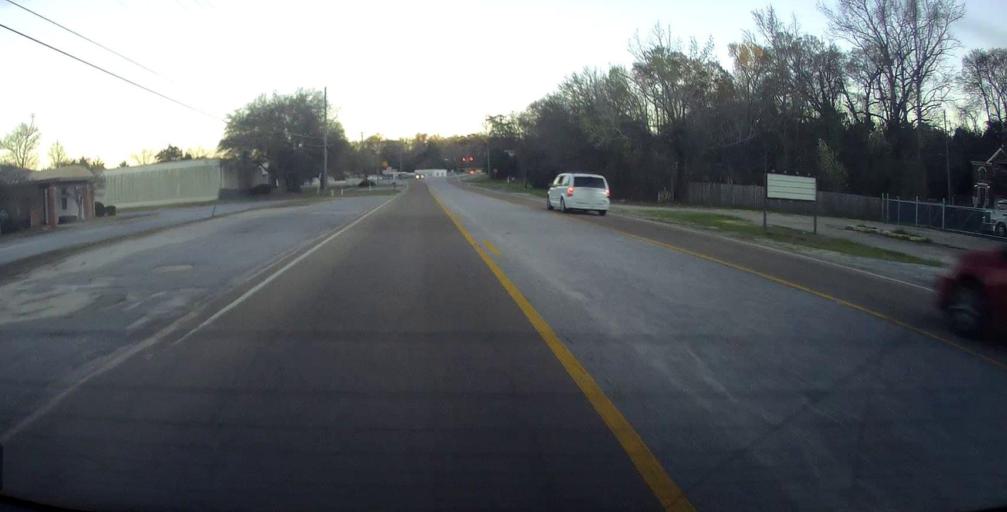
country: US
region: Alabama
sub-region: Russell County
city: Phenix City
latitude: 32.4766
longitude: -85.0253
